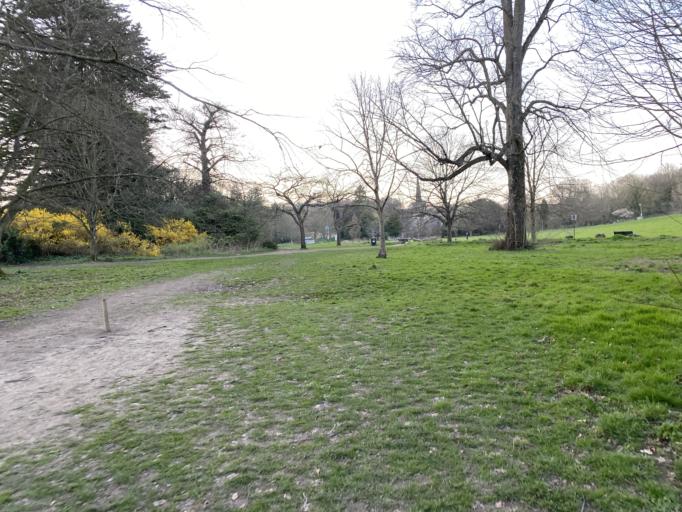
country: GB
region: England
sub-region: Brighton and Hove
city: Brighton
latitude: 50.8686
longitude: -0.1002
